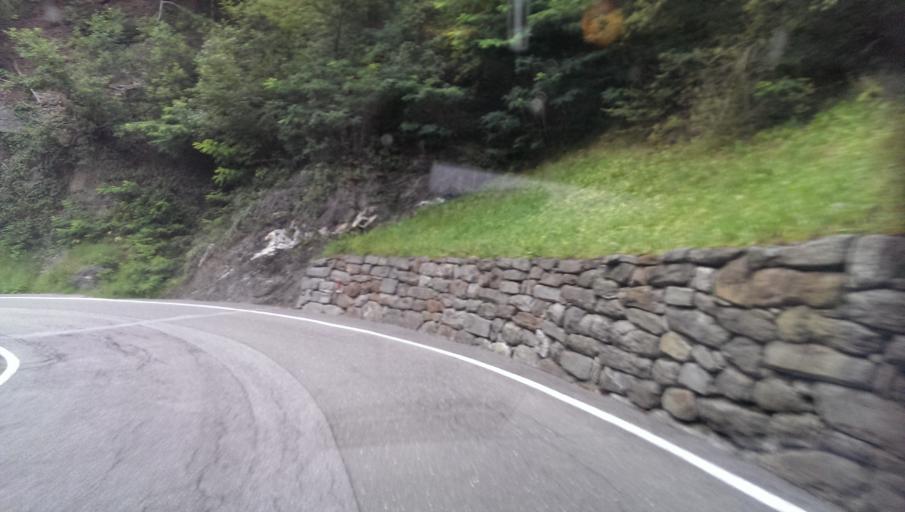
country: IT
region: Trentino-Alto Adige
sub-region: Bolzano
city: San Leonardo in Passiria
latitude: 46.8172
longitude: 11.2488
